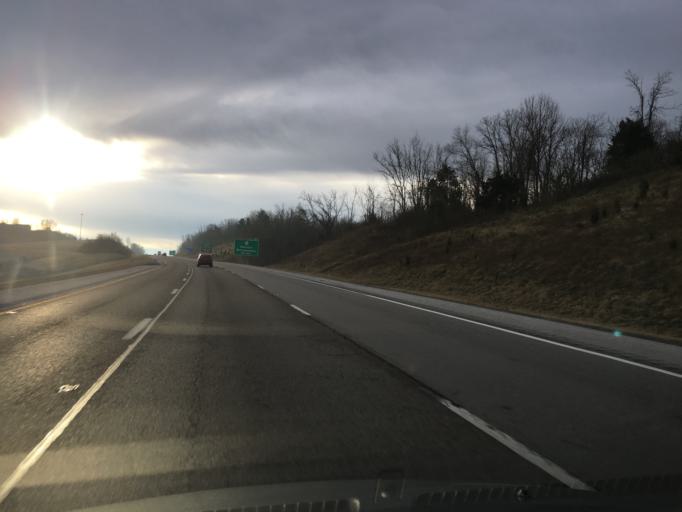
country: US
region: Kentucky
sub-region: Grant County
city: Williamstown
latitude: 38.6349
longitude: -84.5814
